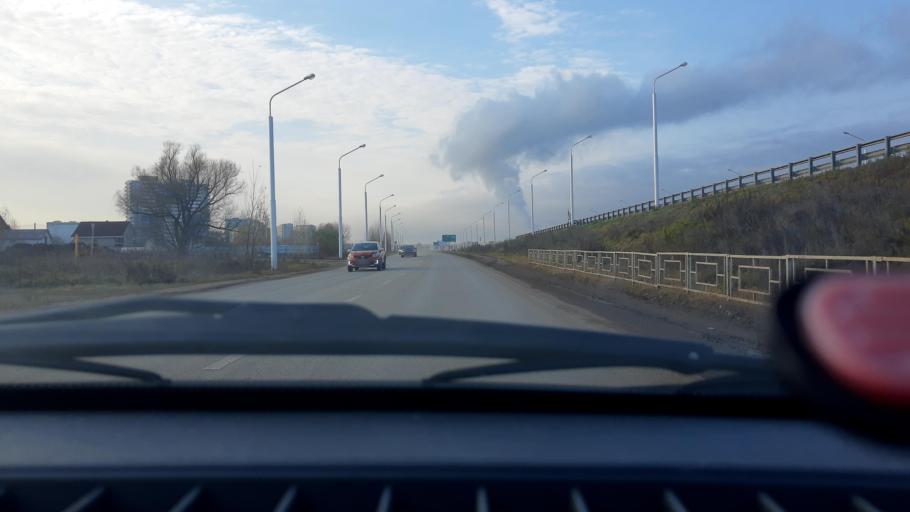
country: RU
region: Bashkortostan
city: Mikhaylovka
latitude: 54.7961
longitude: 55.8873
